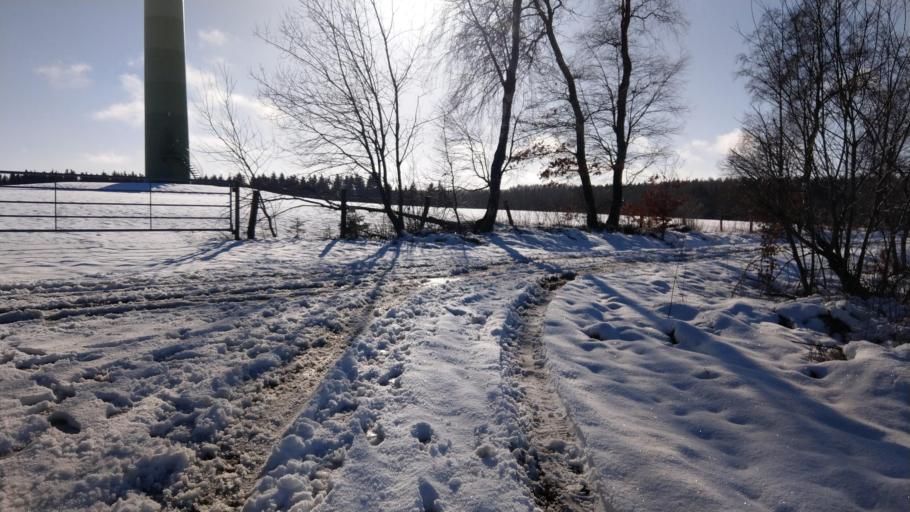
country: DE
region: North Rhine-Westphalia
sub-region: Regierungsbezirk Koln
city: Monschau
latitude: 50.5196
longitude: 6.2852
